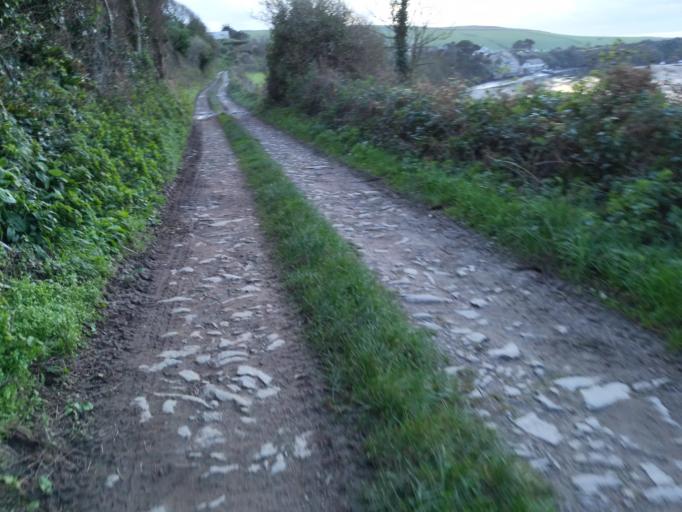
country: GB
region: England
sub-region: Devon
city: Modbury
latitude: 50.2818
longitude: -3.8643
